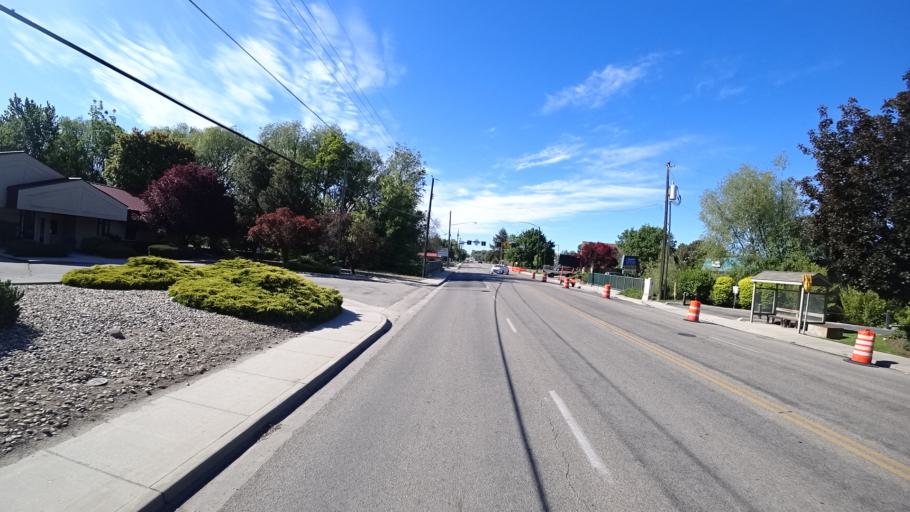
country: US
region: Idaho
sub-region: Ada County
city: Garden City
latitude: 43.5977
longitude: -116.2435
